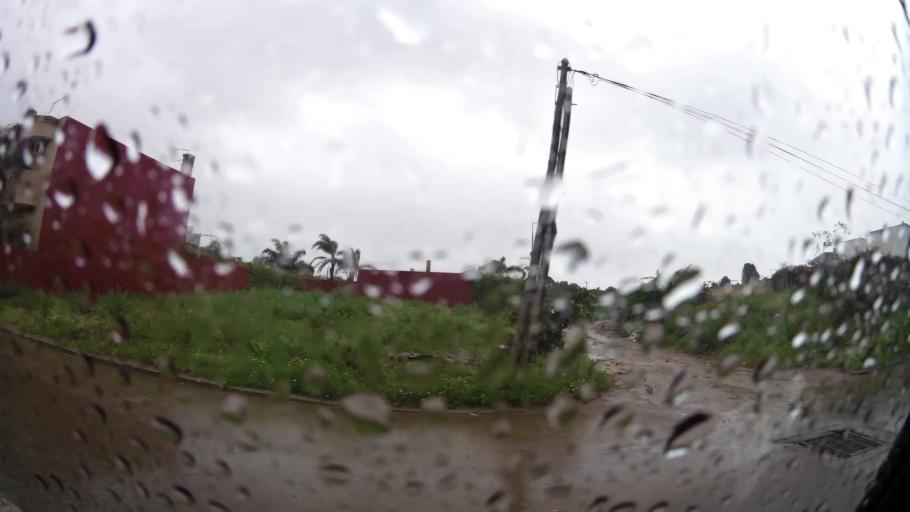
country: MA
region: Grand Casablanca
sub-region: Casablanca
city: Casablanca
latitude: 33.5433
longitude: -7.6698
